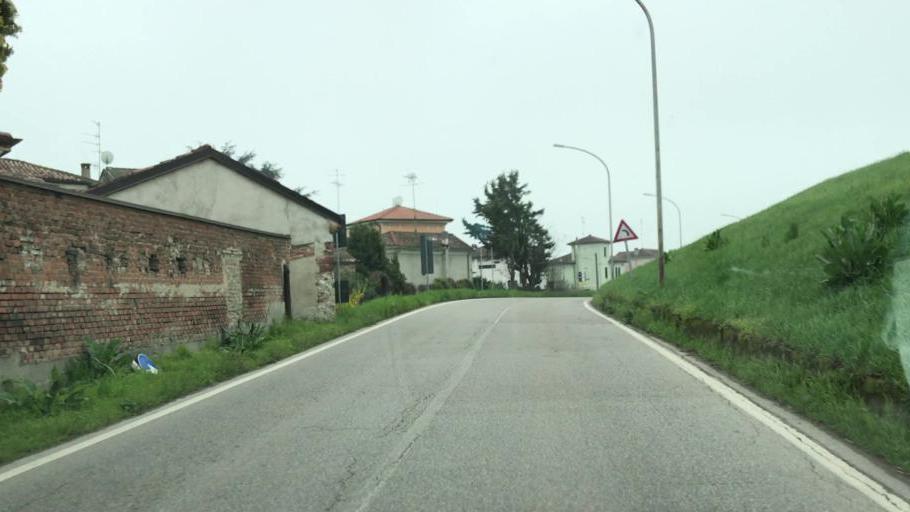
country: IT
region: Lombardy
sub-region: Provincia di Mantova
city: San Benedetto Po
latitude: 45.0416
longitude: 10.9261
